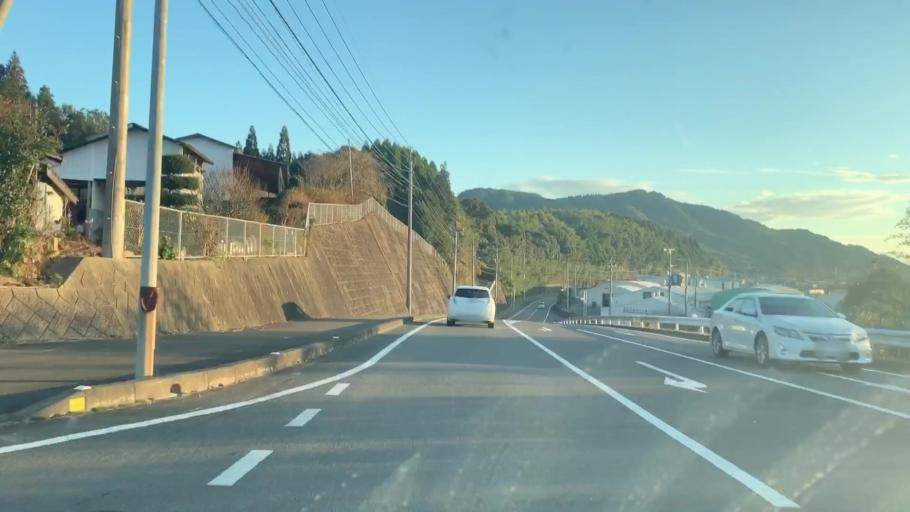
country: JP
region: Saga Prefecture
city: Imaricho-ko
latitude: 33.2911
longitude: 129.9705
